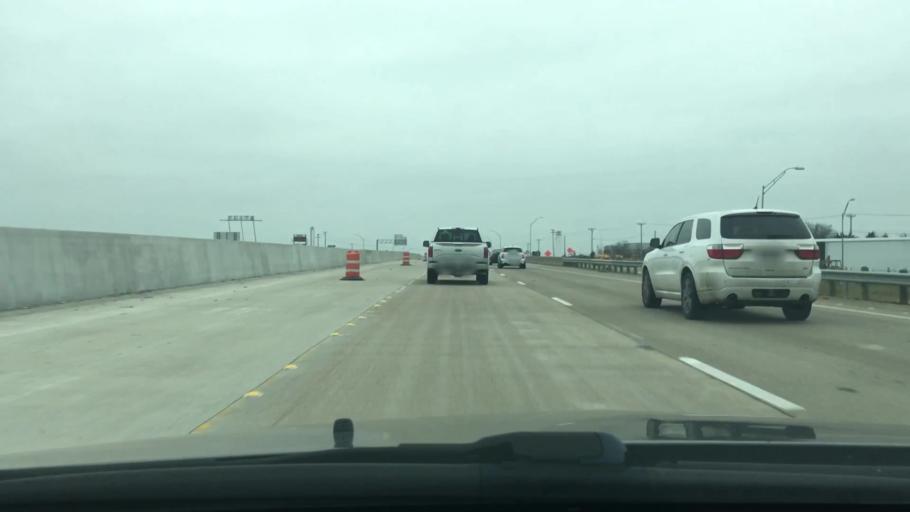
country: US
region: Texas
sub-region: Navarro County
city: Corsicana
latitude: 32.0606
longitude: -96.4523
